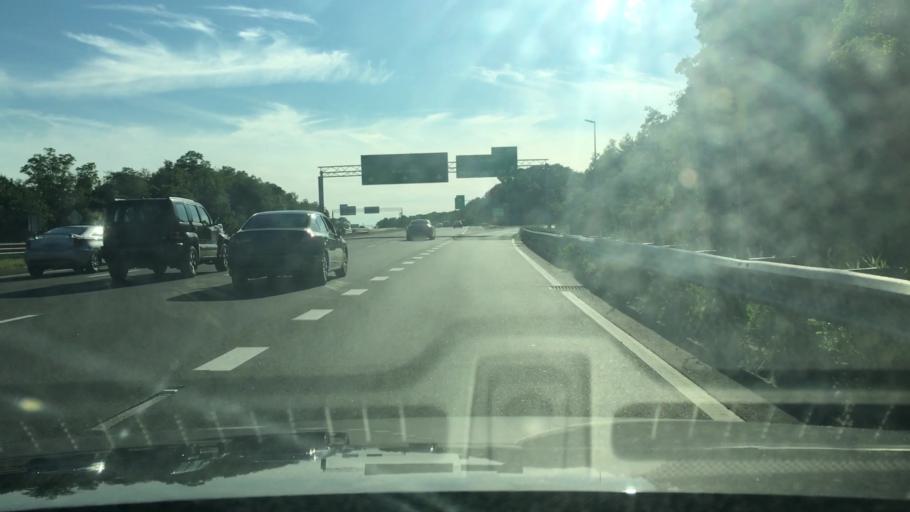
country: US
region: Massachusetts
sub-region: Essex County
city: South Peabody
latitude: 42.5260
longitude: -70.9671
